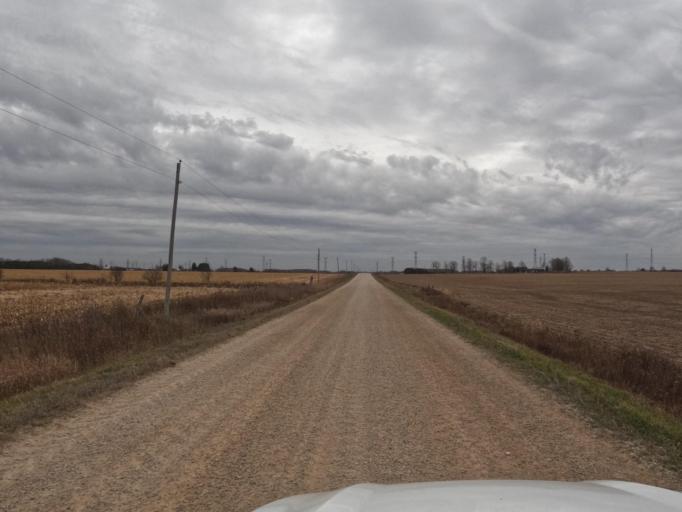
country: CA
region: Ontario
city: Shelburne
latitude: 43.9993
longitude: -80.3868
